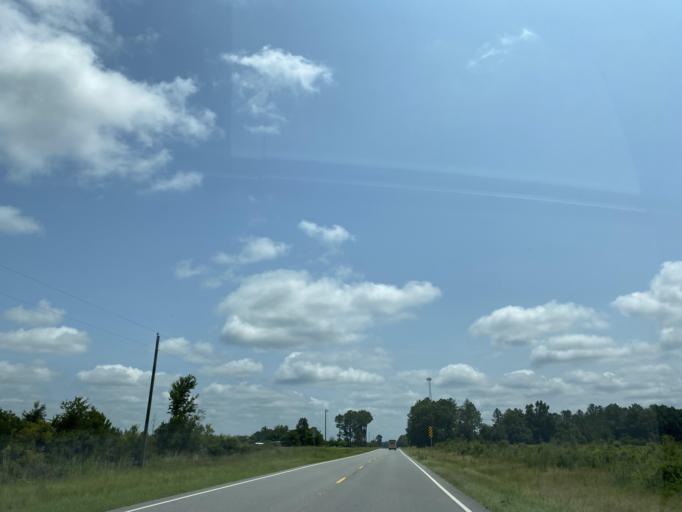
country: US
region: Georgia
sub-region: Jeff Davis County
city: Hazlehurst
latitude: 31.7336
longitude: -82.5345
